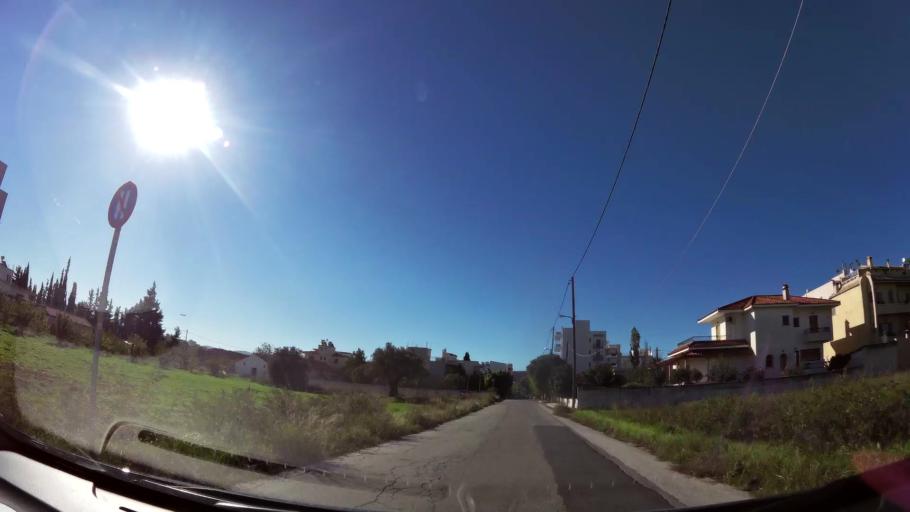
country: GR
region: Attica
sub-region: Nomarchia Anatolikis Attikis
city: Koropi
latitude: 37.9081
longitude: 23.8698
